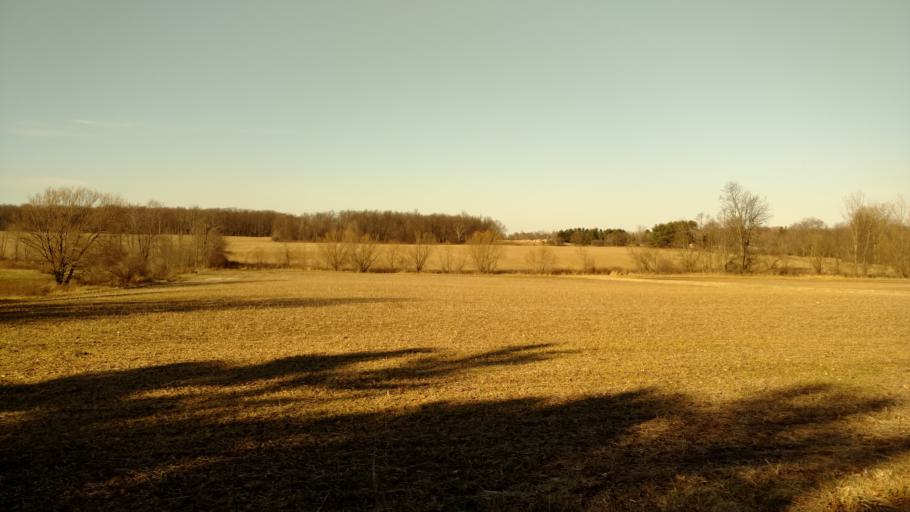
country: US
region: Ohio
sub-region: Crawford County
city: Galion
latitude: 40.6972
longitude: -82.7695
